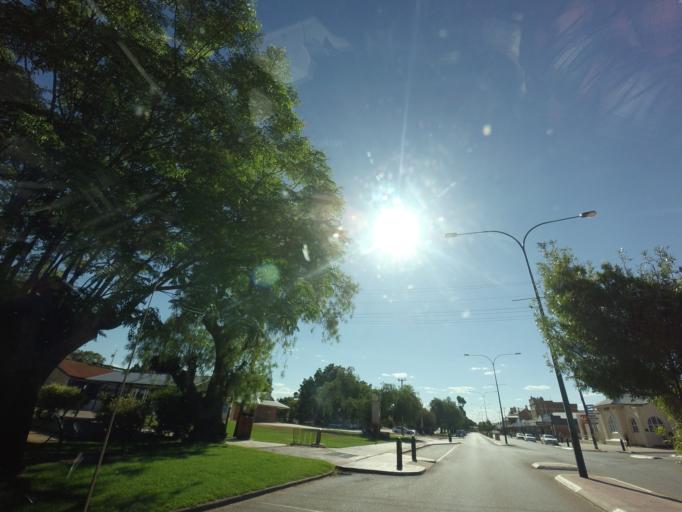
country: AU
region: Western Australia
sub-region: Merredin
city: Merredin
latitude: -31.4822
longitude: 118.2790
